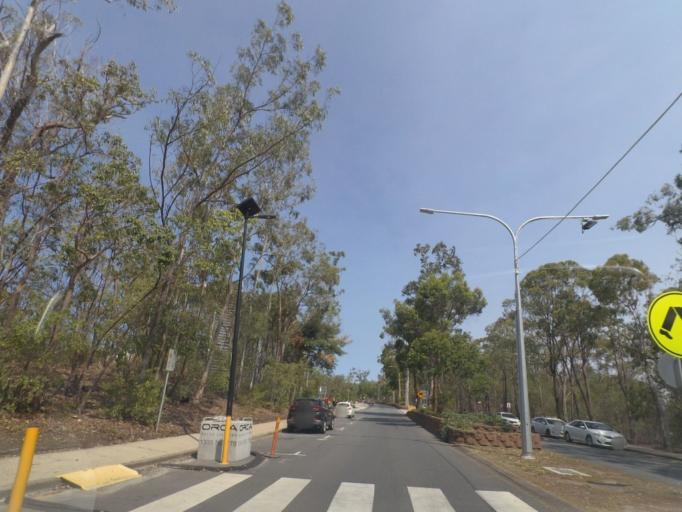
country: AU
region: Queensland
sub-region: Brisbane
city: Nathan
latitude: -27.5527
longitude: 153.0504
